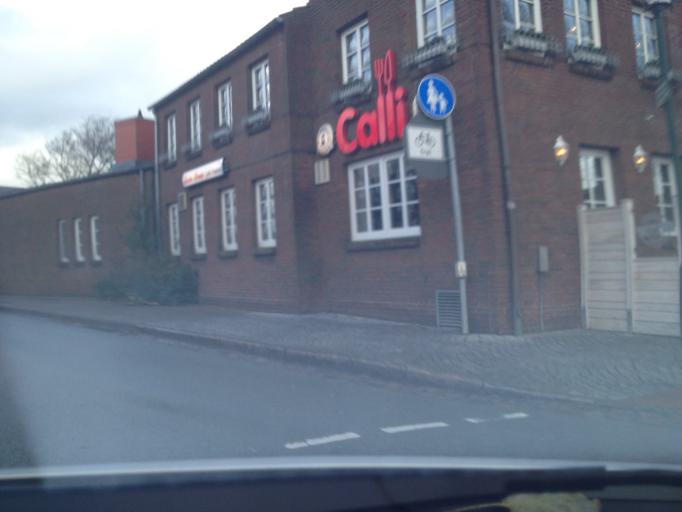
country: DE
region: Schleswig-Holstein
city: Leck
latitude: 54.7720
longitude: 8.9745
